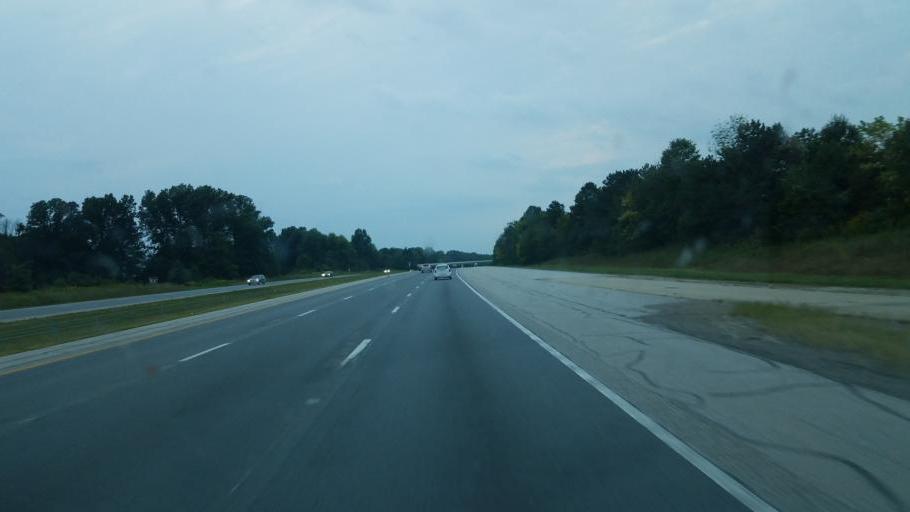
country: US
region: Ohio
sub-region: Ashland County
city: Ashland
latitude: 40.8814
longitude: -82.1990
